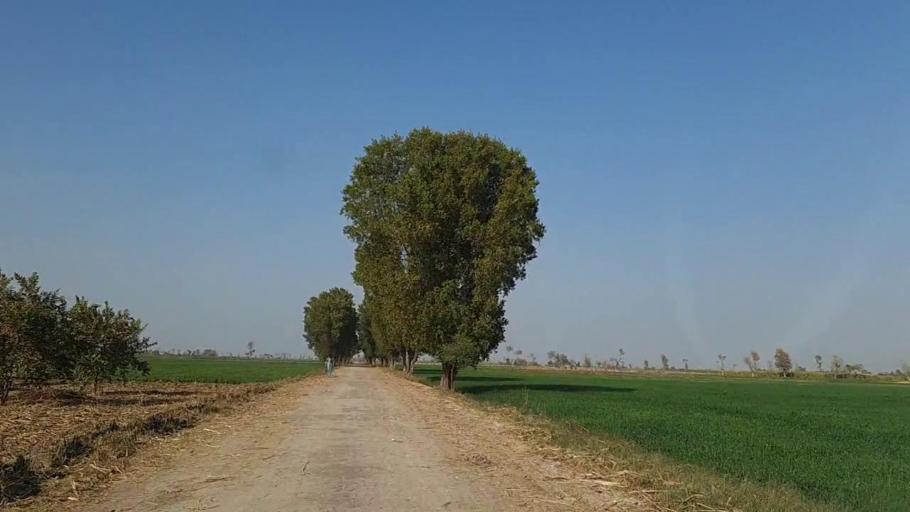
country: PK
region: Sindh
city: Daur
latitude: 26.4830
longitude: 68.2973
